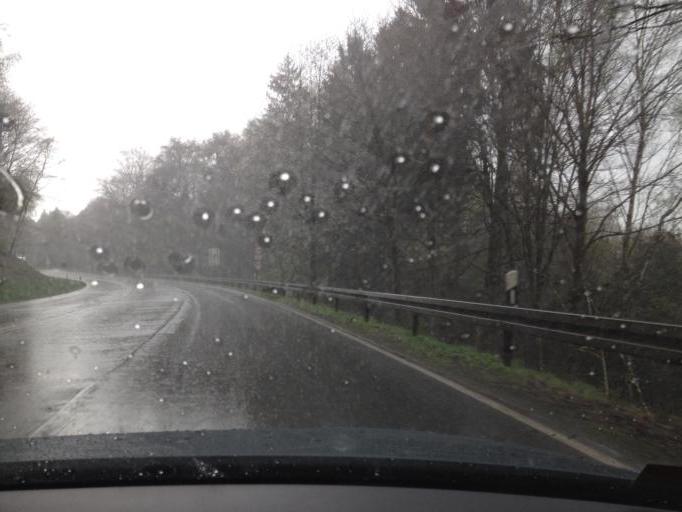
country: DE
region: Saarland
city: Ottweiler
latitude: 49.3932
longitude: 7.1581
